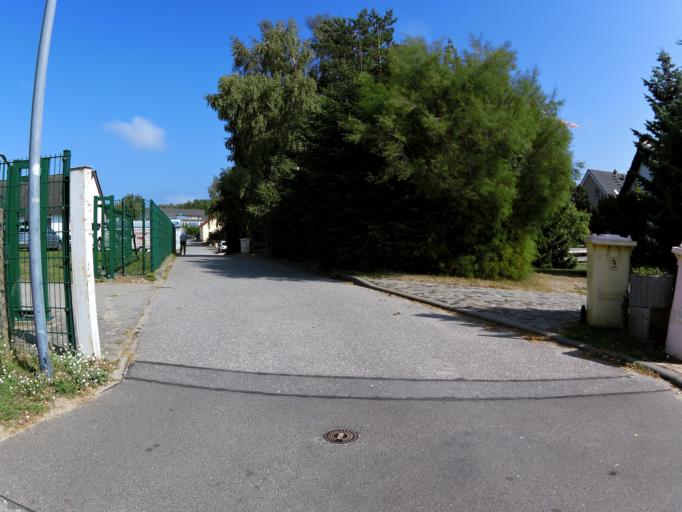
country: DE
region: Mecklenburg-Vorpommern
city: Loddin
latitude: 54.0107
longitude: 14.0492
